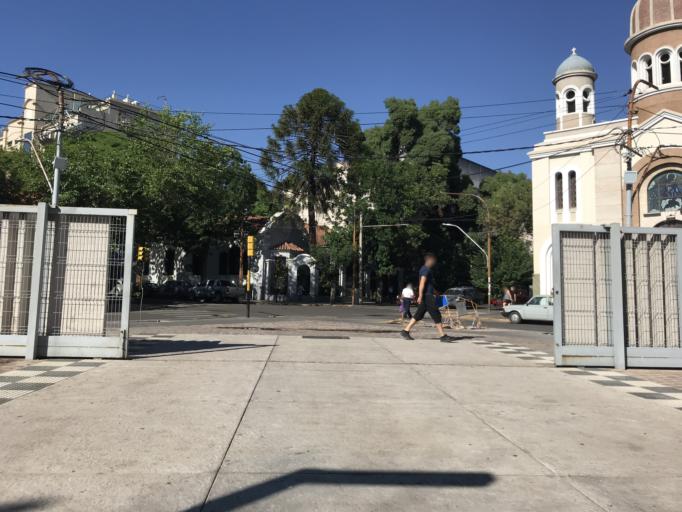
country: AR
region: Mendoza
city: Mendoza
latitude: -32.8885
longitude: -68.8324
